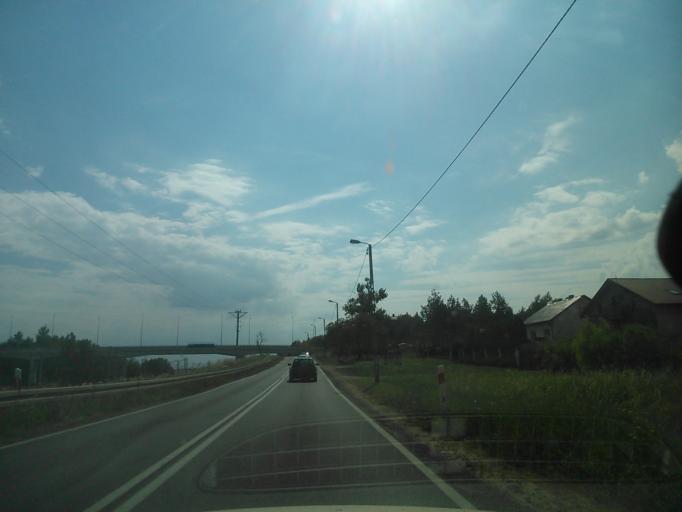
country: PL
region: Warmian-Masurian Voivodeship
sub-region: Powiat dzialdowski
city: Ilowo -Osada
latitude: 53.1438
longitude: 20.3393
